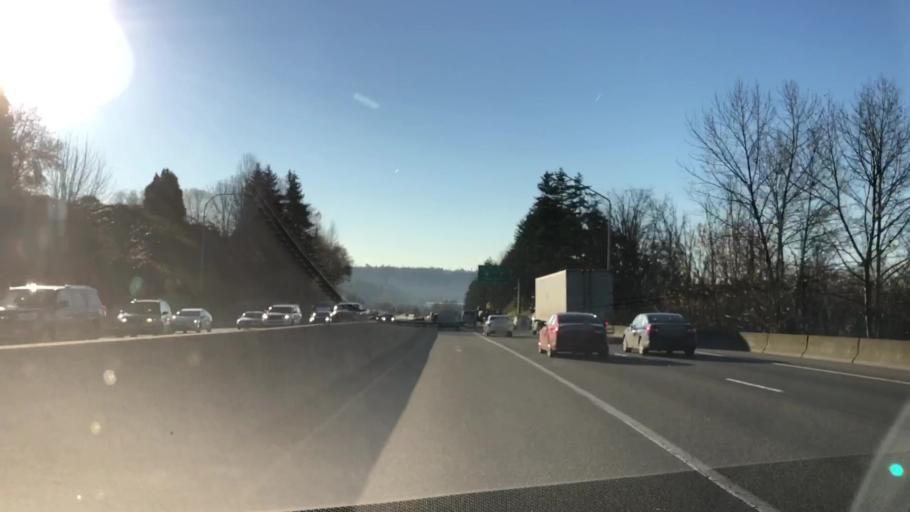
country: US
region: Washington
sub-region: King County
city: Renton
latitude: 47.5080
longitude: -122.1991
